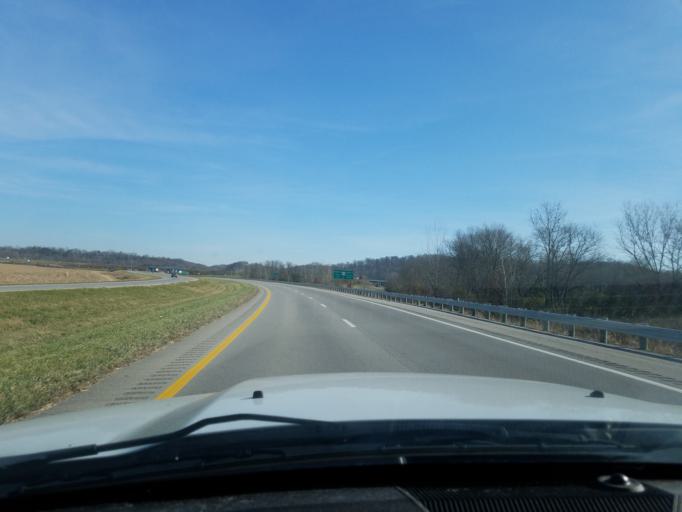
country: US
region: Ohio
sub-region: Pike County
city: Piketon
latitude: 39.0461
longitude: -83.0328
